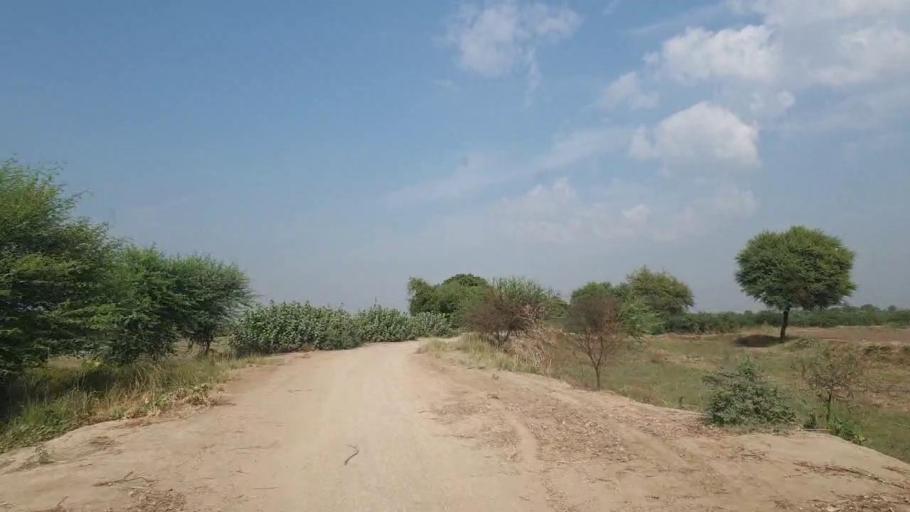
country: PK
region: Sindh
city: Digri
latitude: 25.0163
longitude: 69.0673
